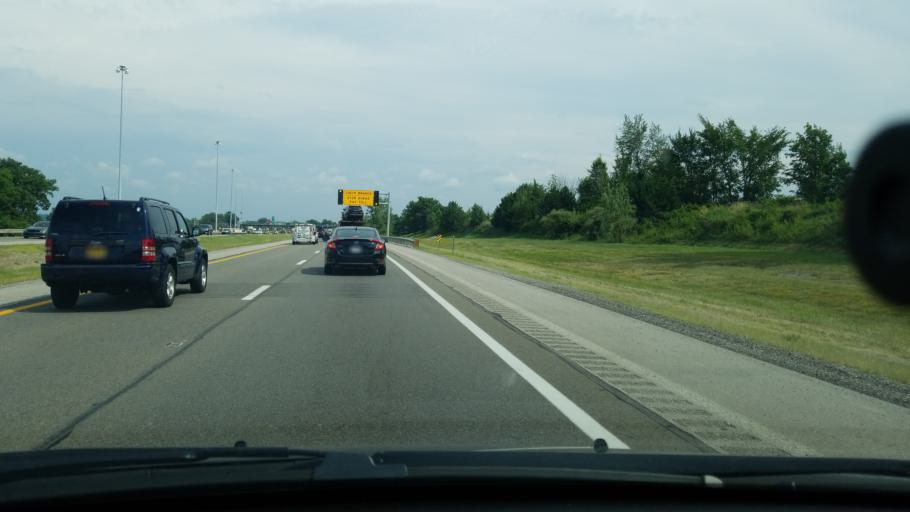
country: US
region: Ohio
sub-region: Mahoning County
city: New Middletown
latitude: 40.9269
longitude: -80.5623
